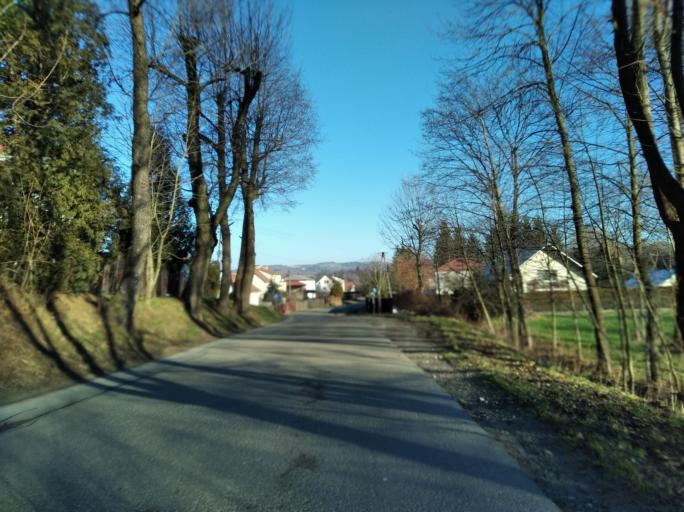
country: PL
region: Subcarpathian Voivodeship
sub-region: Powiat strzyzowski
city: Strzyzow
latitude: 49.8596
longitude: 21.7877
